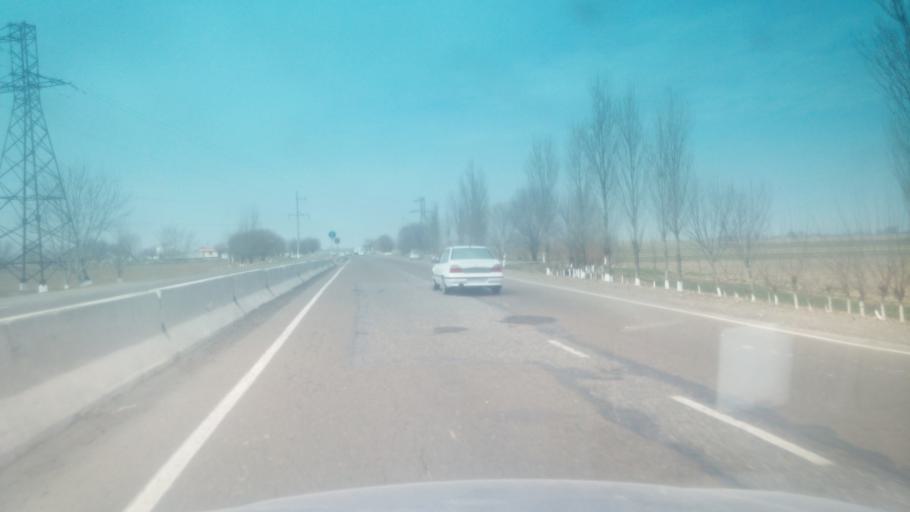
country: KZ
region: Ongtustik Qazaqstan
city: Myrzakent
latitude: 40.5237
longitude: 68.4553
